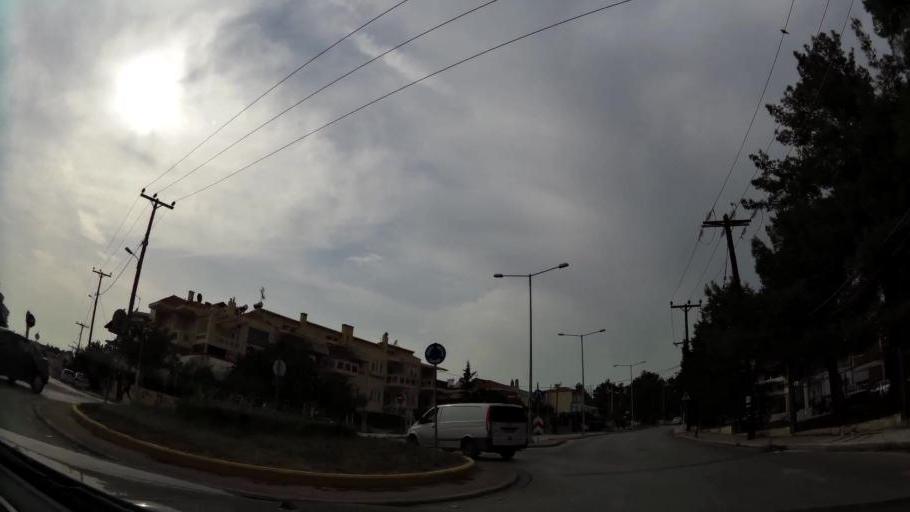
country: GR
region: Central Macedonia
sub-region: Nomos Thessalonikis
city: Oraiokastro
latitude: 40.7255
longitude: 22.9234
